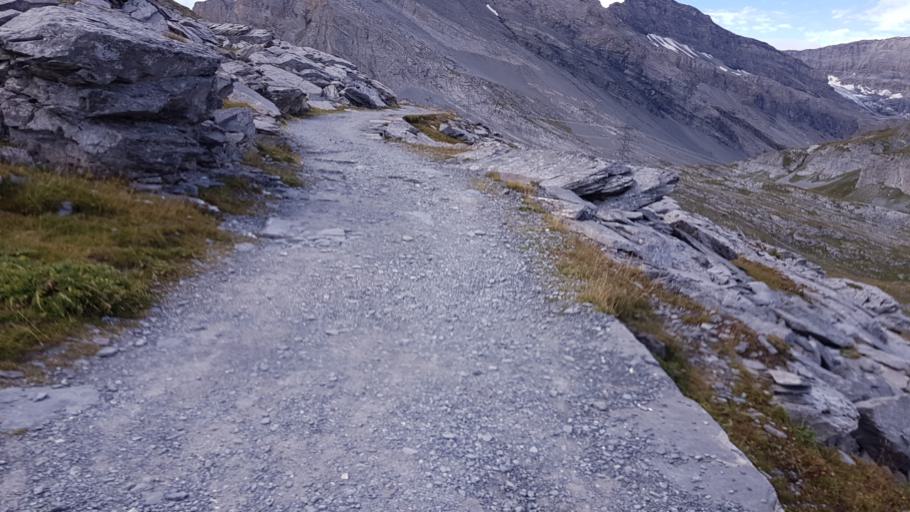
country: CH
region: Valais
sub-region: Leuk District
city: Leukerbad
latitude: 46.4029
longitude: 7.6185
